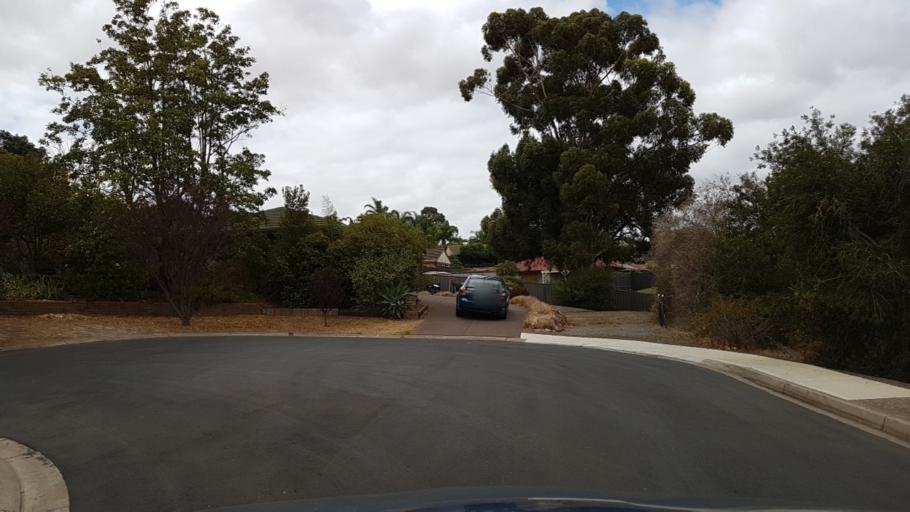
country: AU
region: South Australia
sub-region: Gawler
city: Gawler
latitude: -34.6055
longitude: 138.7589
